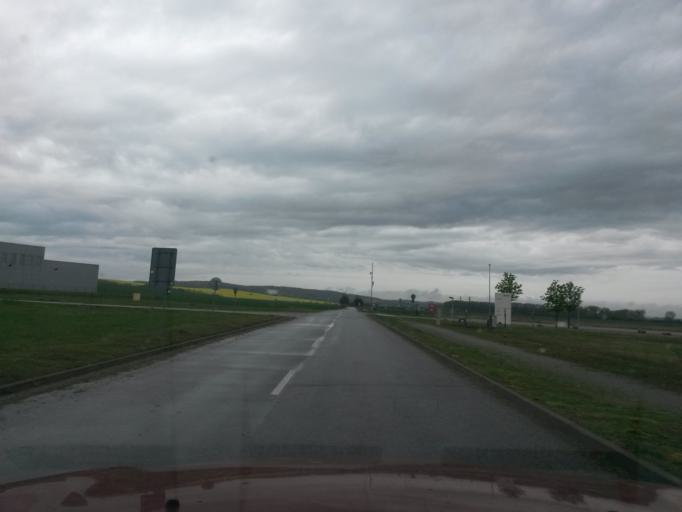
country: HU
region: Borsod-Abauj-Zemplen
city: Gonc
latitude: 48.5477
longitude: 21.2270
